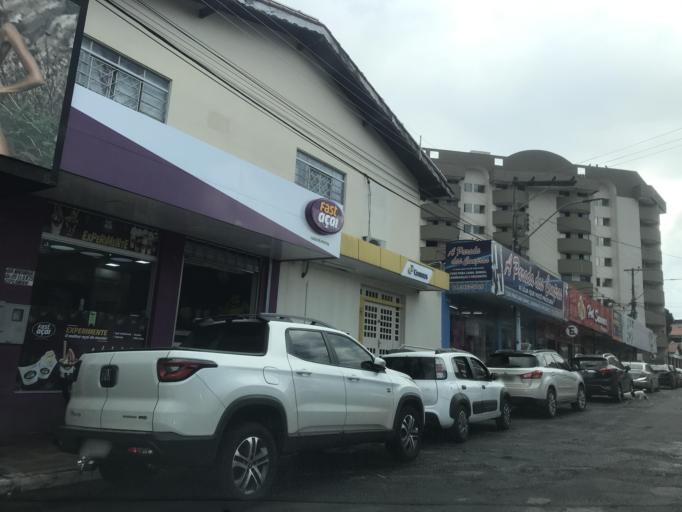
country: BR
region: Goias
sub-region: Caldas Novas
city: Caldas Novas
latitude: -17.7708
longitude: -48.7550
